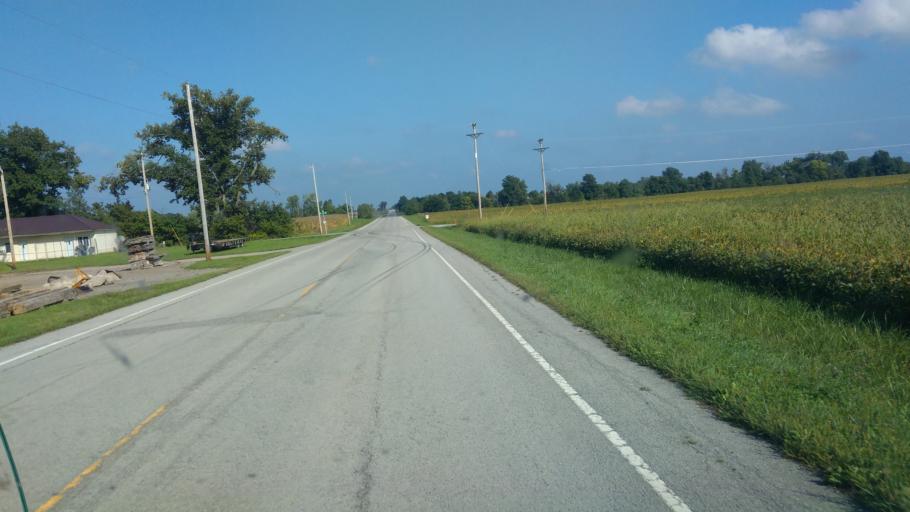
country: US
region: Ohio
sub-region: Hancock County
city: Arlington
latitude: 40.8341
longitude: -83.6716
